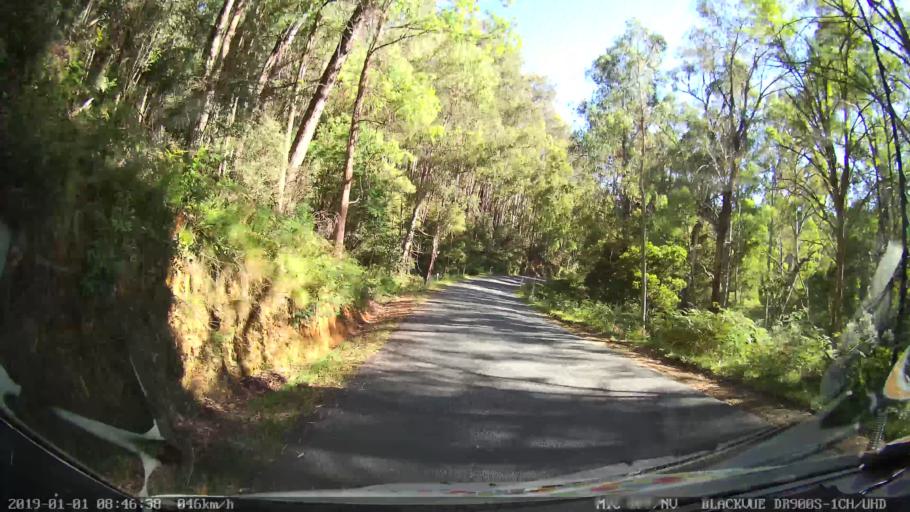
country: AU
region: New South Wales
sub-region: Snowy River
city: Jindabyne
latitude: -36.2991
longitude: 148.1941
